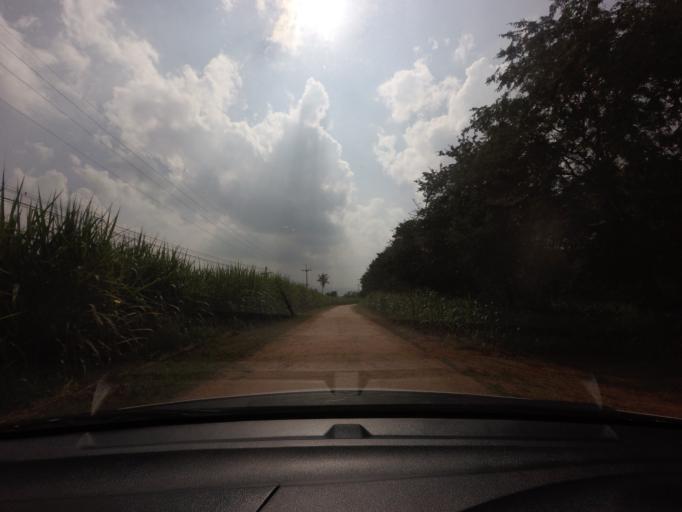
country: TH
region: Nakhon Ratchasima
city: Pak Chong
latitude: 14.5338
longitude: 101.5883
